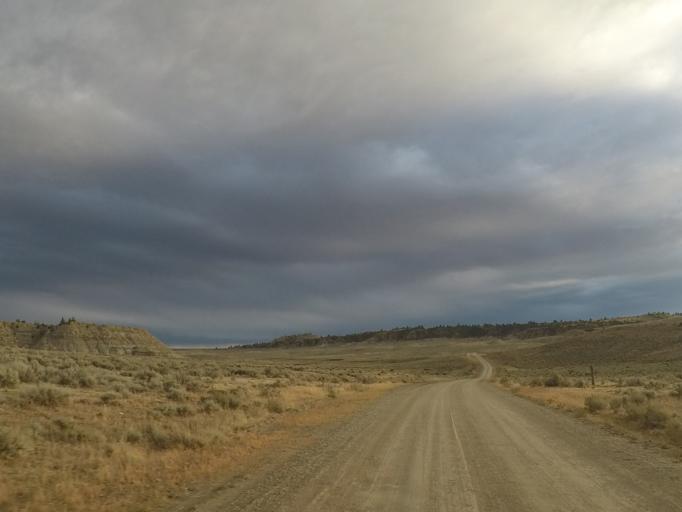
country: US
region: Montana
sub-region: Golden Valley County
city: Ryegate
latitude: 46.4458
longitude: -109.2572
